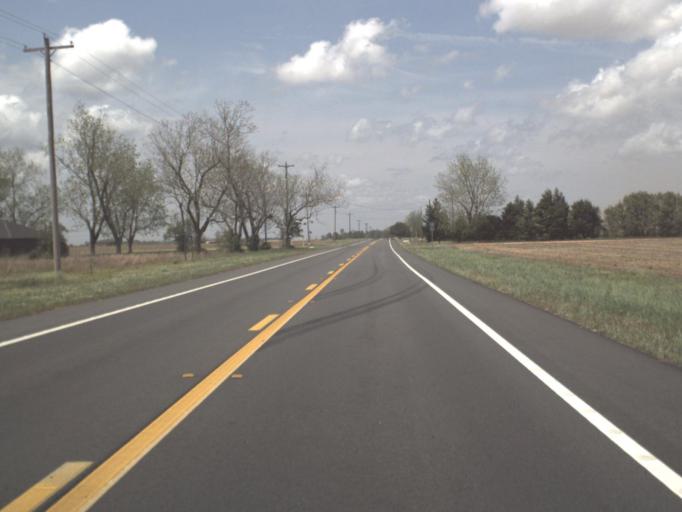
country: US
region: Florida
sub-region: Escambia County
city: Century
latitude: 30.8792
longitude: -87.1614
